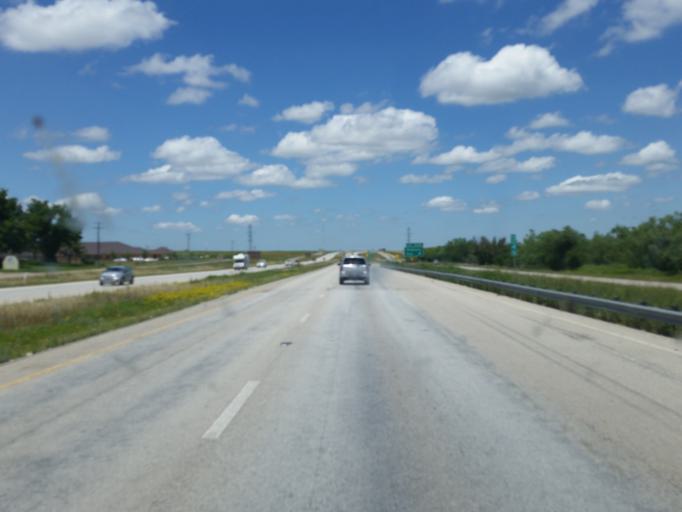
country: US
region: Texas
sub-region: Nolan County
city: Sweetwater
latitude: 32.4595
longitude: -100.3861
